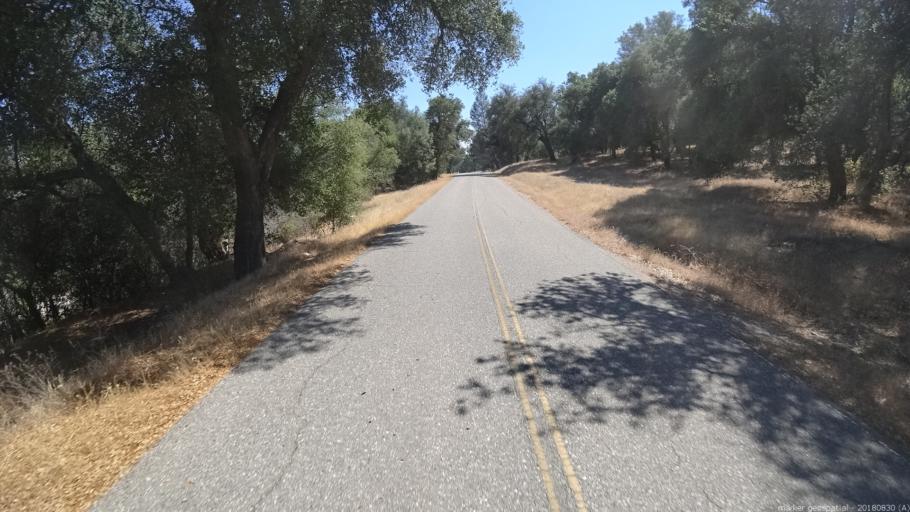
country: US
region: California
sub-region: Monterey County
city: King City
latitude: 36.0667
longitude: -121.3145
